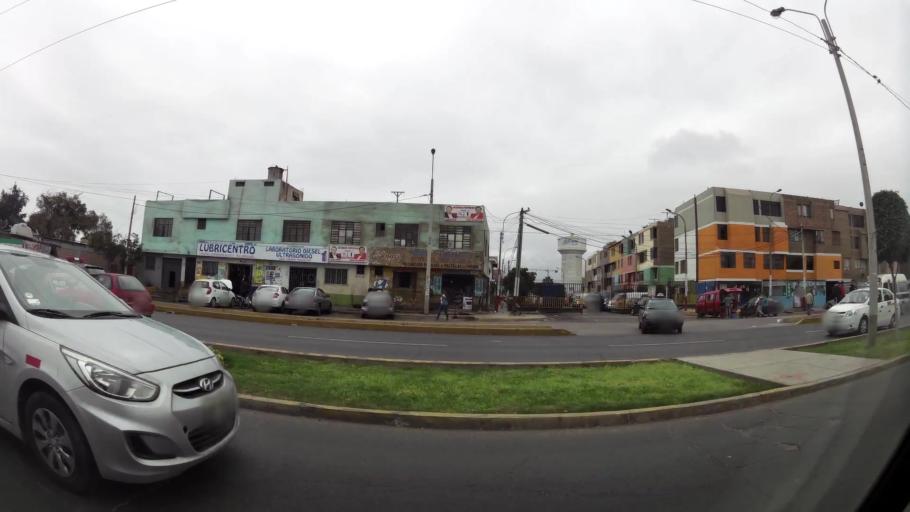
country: PE
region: Callao
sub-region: Callao
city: Callao
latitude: -12.0574
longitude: -77.1165
